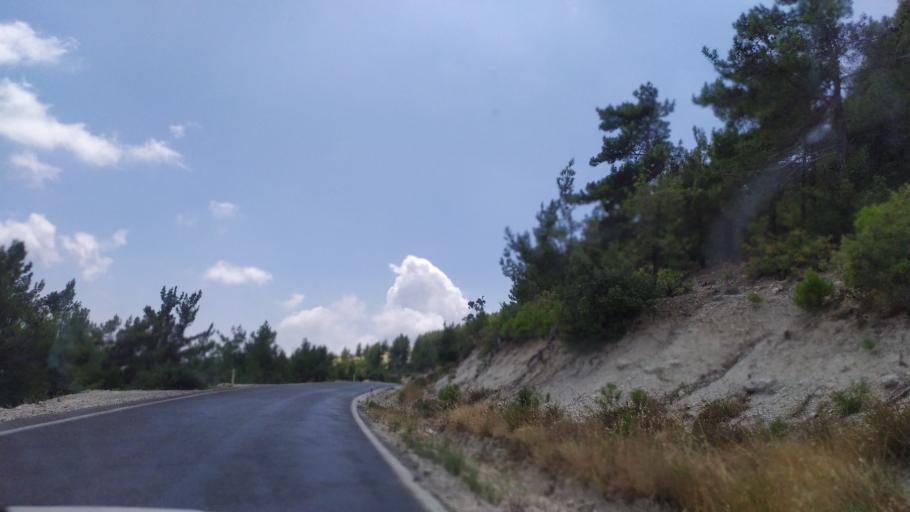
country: TR
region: Mersin
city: Gulnar
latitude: 36.2930
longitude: 33.3801
